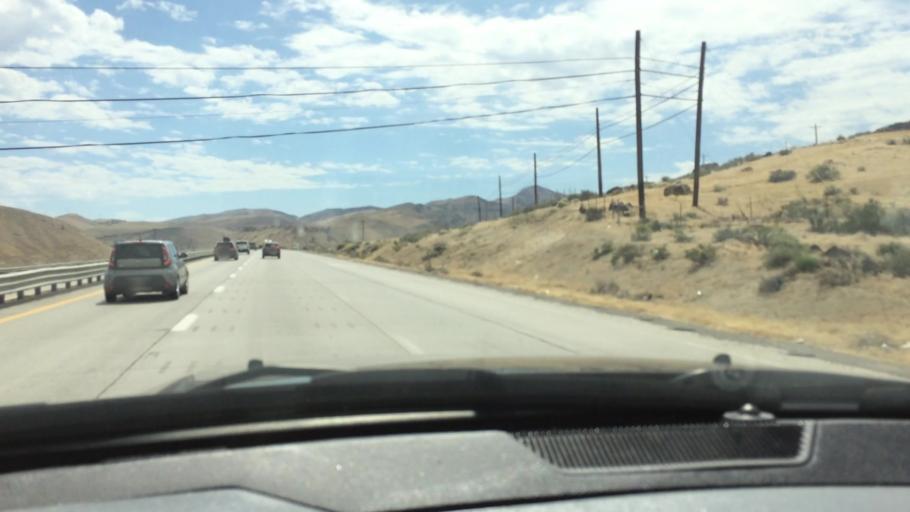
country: US
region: Nevada
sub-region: Washoe County
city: Sparks
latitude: 39.5173
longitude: -119.6326
